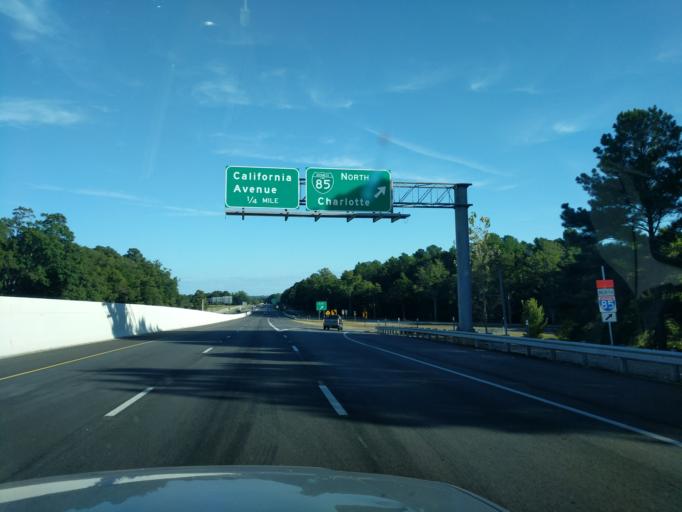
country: US
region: South Carolina
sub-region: Spartanburg County
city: Saxon
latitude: 34.9889
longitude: -81.9649
